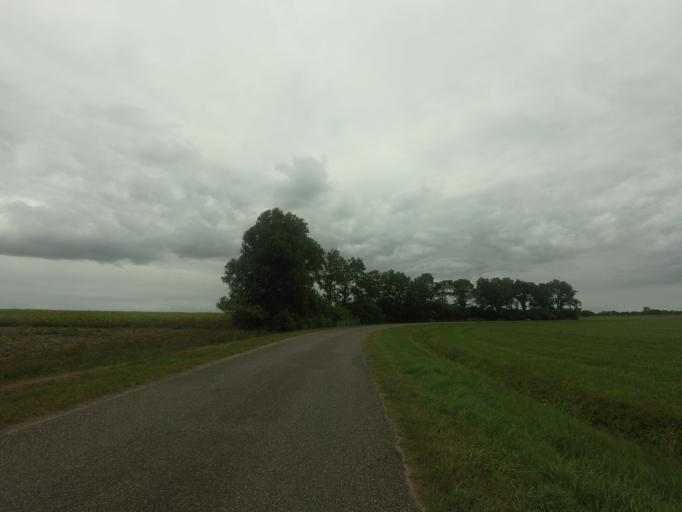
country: NL
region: Drenthe
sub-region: Gemeente Westerveld
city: Dwingeloo
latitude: 52.9652
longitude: 6.3142
